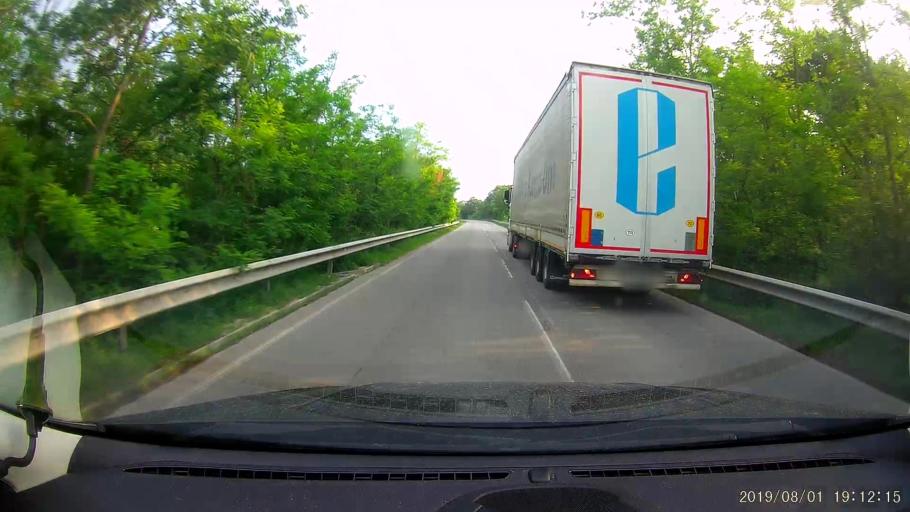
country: BG
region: Shumen
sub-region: Obshtina Smyadovo
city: Smyadovo
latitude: 42.9659
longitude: 26.9517
